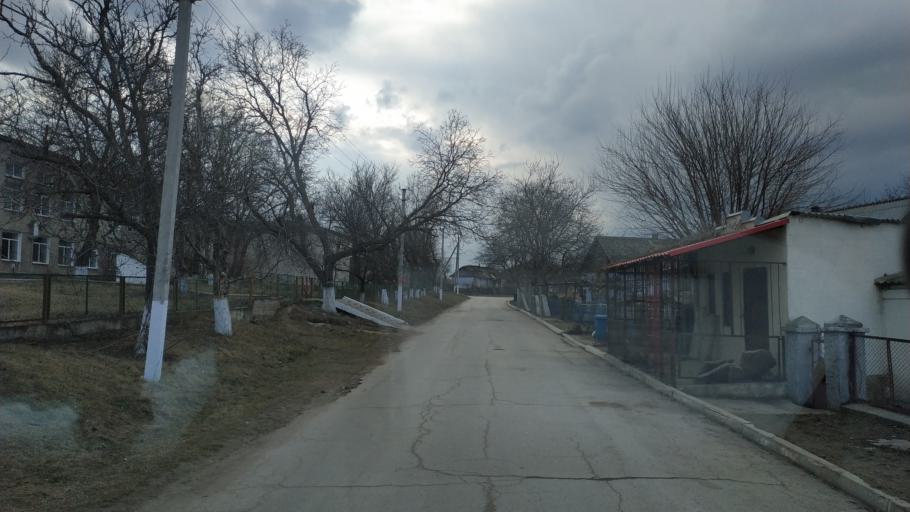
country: MD
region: Anenii Noi
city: Anenii Noi
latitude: 46.8855
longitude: 29.3104
